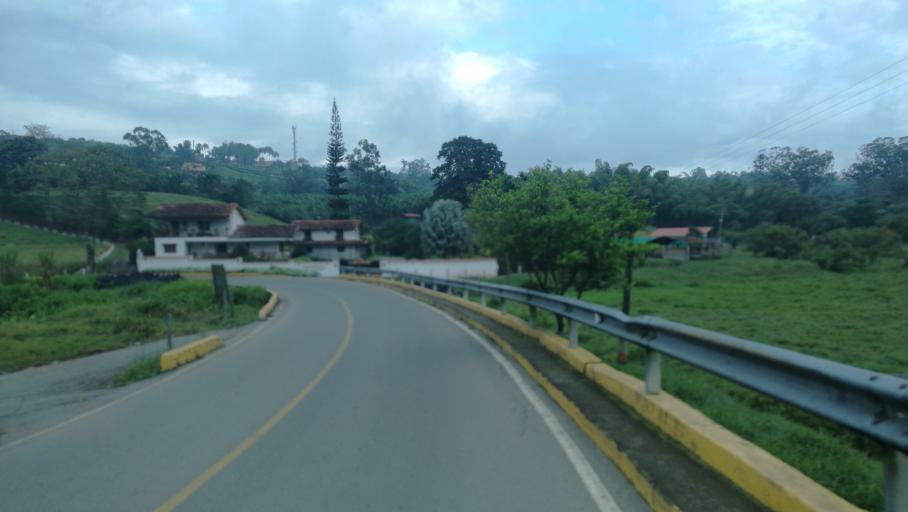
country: CO
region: Quindio
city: La Tebaida
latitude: 4.5100
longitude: -75.7794
